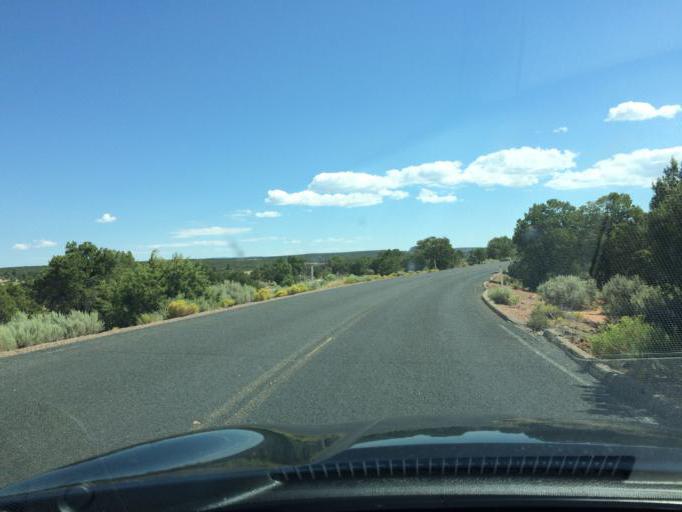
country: US
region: Arizona
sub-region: Apache County
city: Chinle
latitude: 36.1037
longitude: -109.3702
